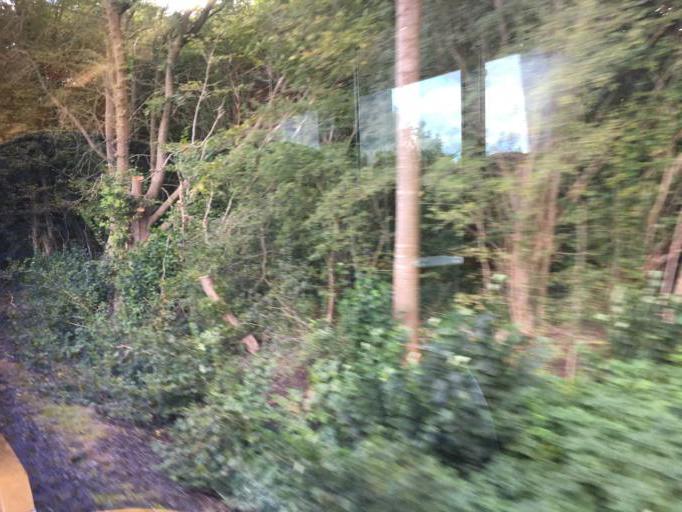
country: DE
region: Schleswig-Holstein
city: Kronshagen
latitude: 54.3125
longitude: 10.0818
